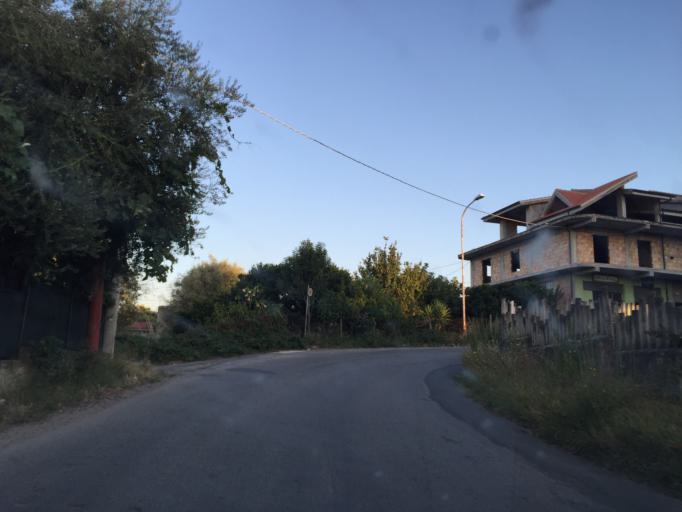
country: IT
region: Calabria
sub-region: Provincia di Vibo-Valentia
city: Pannaconi
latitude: 38.6938
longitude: 16.0449
